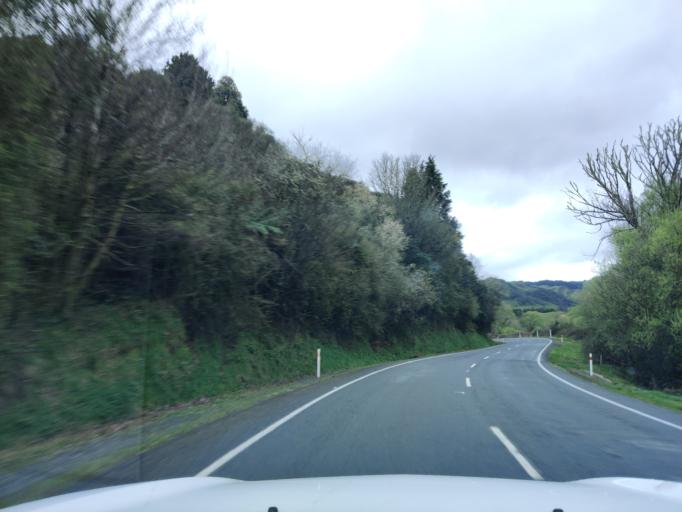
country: NZ
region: Waikato
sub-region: Otorohanga District
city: Otorohanga
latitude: -38.5978
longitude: 175.2173
